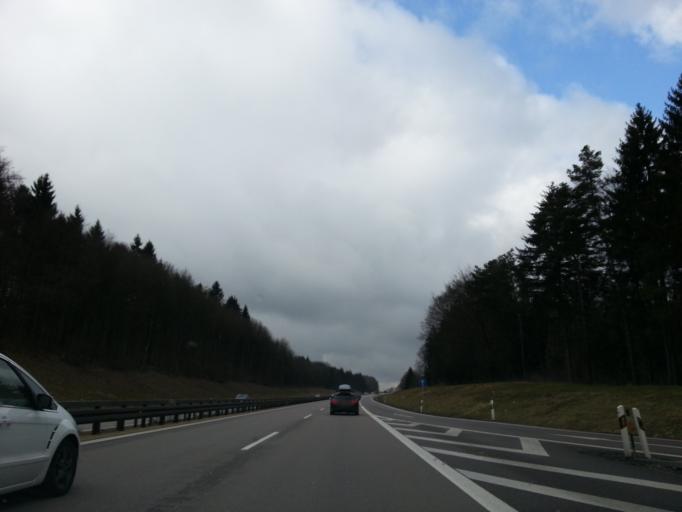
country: DE
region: Bavaria
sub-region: Upper Palatinate
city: Brunn
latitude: 49.1178
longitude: 11.8724
